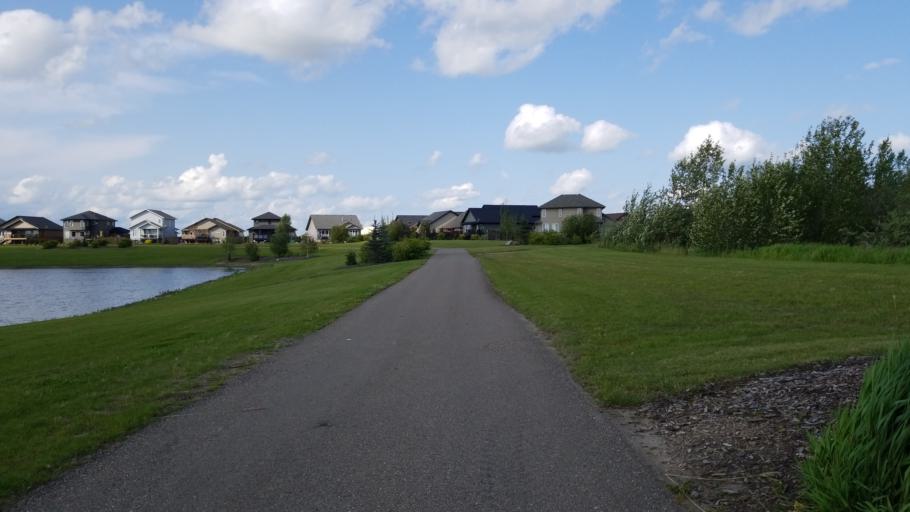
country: CA
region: Saskatchewan
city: Lloydminster
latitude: 53.2626
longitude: -110.0467
